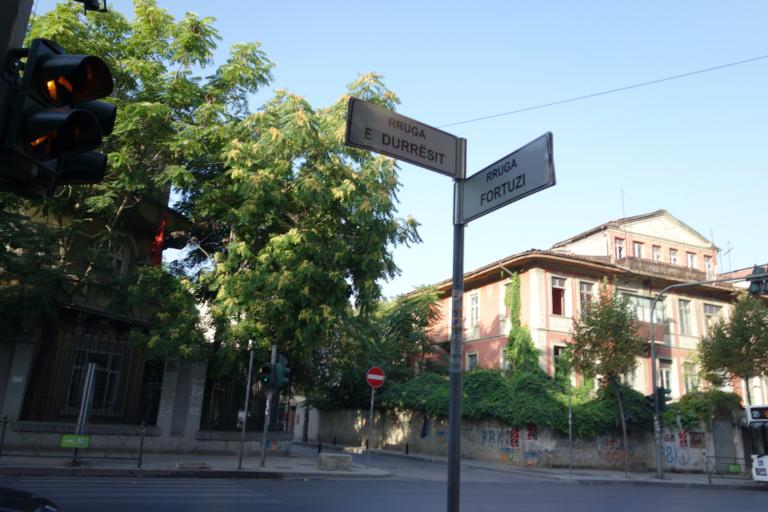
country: AL
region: Tirane
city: Tirana
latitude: 41.3303
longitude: 19.8122
